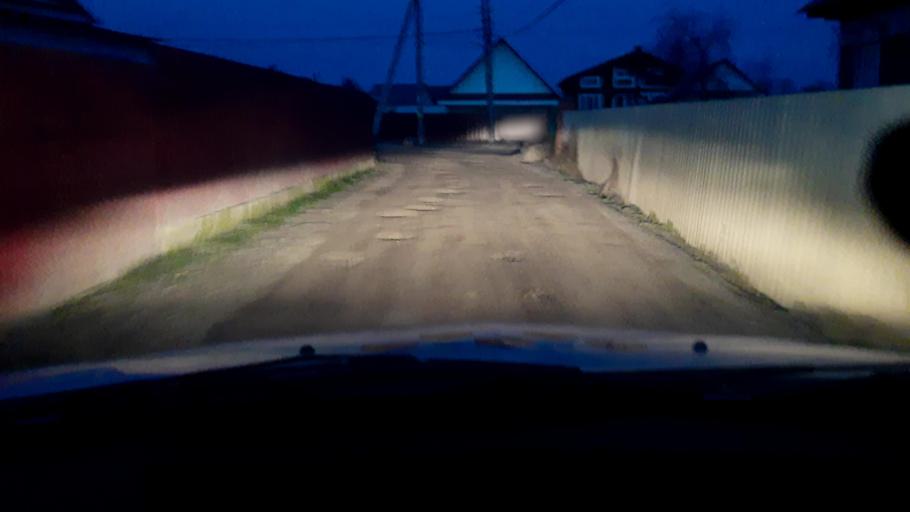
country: RU
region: Bashkortostan
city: Iglino
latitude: 54.7739
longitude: 56.2174
